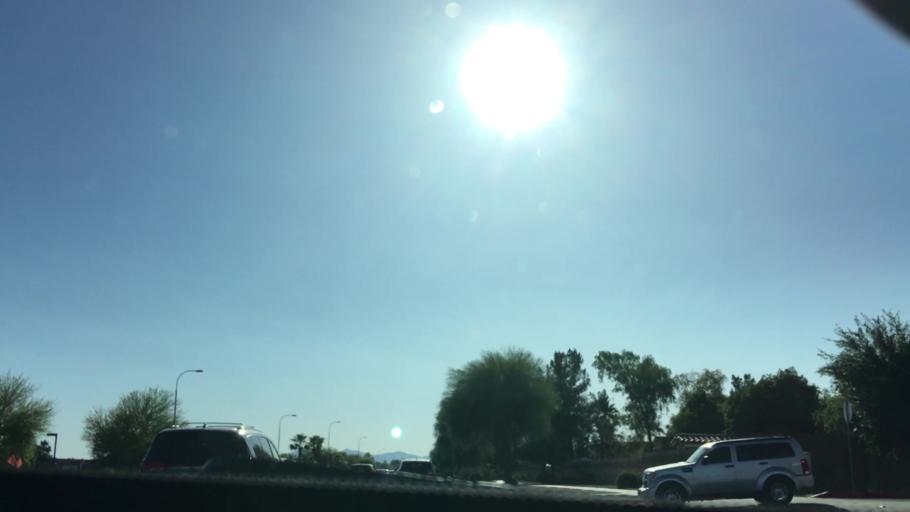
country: US
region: Arizona
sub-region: Maricopa County
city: Peoria
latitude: 33.6106
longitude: -112.2227
